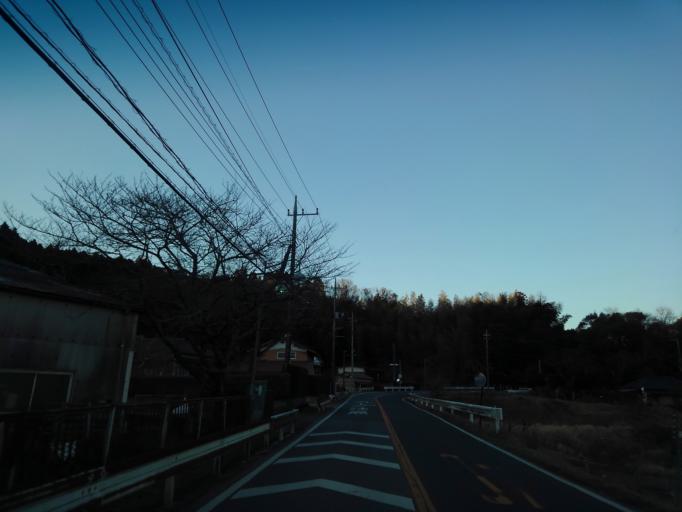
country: JP
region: Chiba
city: Kimitsu
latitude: 35.2916
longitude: 139.9773
